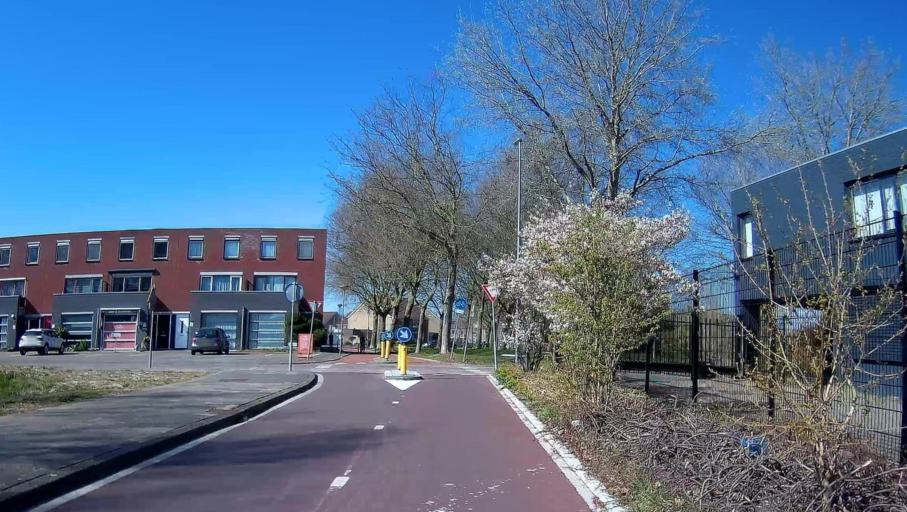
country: NL
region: South Holland
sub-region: Gemeente Capelle aan den IJssel
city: Capelle aan den IJssel
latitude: 51.9582
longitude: 4.5676
